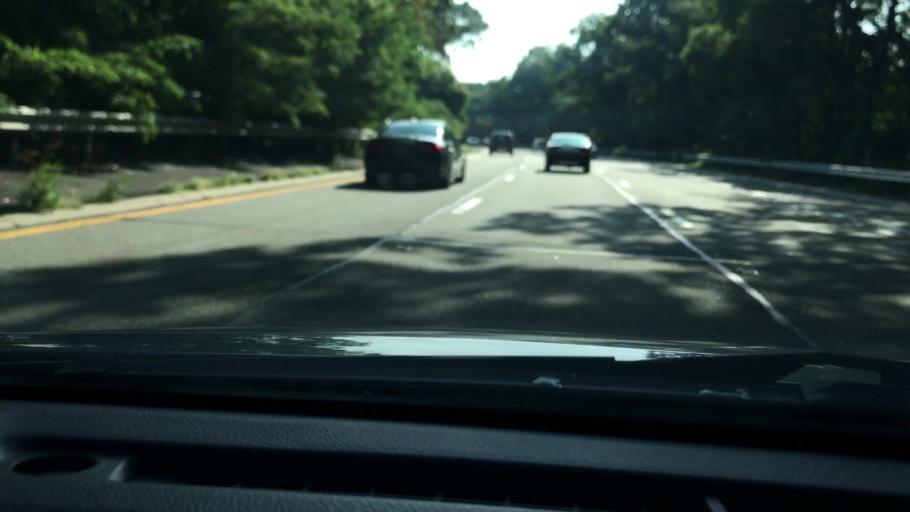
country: US
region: New York
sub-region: Nassau County
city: Lakeview
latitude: 40.6827
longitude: -73.6505
